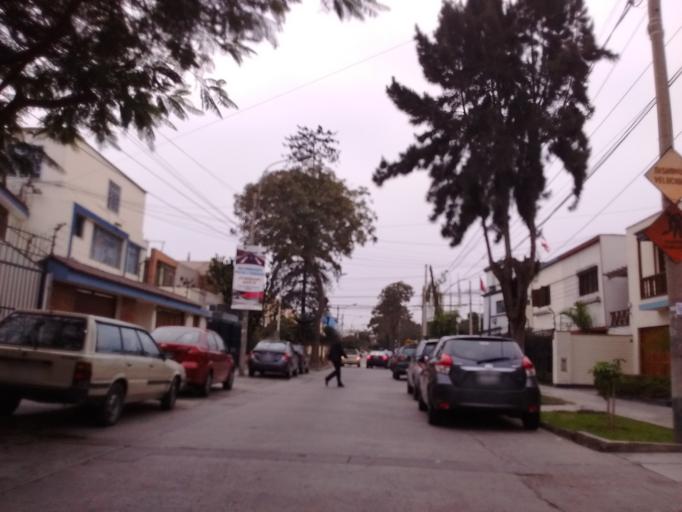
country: PE
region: Lima
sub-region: Lima
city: San Isidro
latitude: -12.0849
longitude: -77.0544
